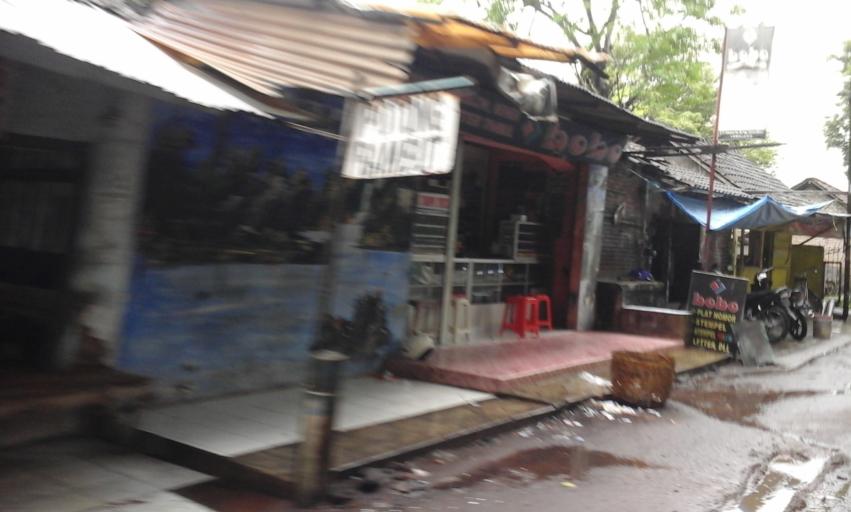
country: ID
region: East Java
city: Rogotrunan
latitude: -8.1253
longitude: 113.2241
